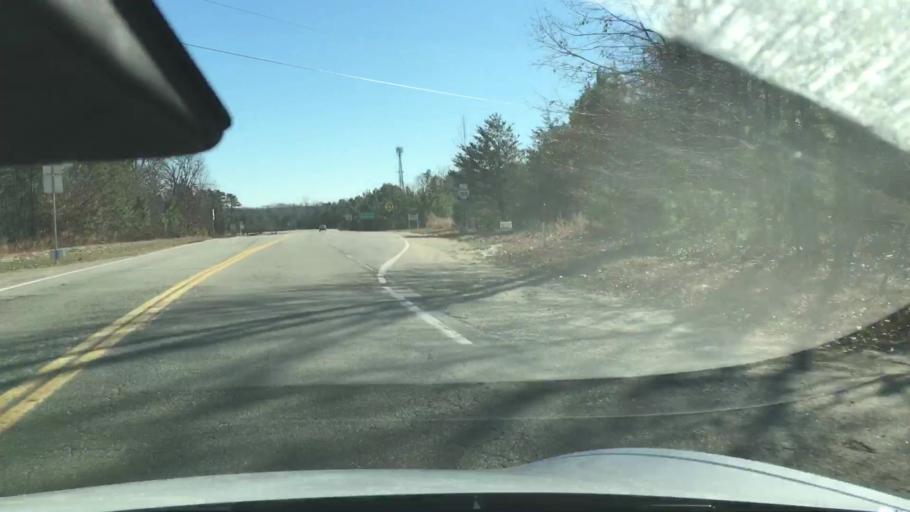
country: US
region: Virginia
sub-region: Henrico County
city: Short Pump
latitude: 37.5614
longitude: -77.6963
